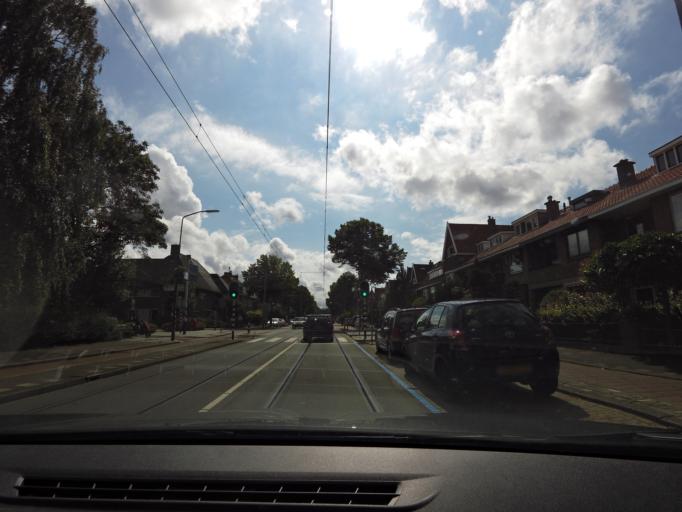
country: NL
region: South Holland
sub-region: Gemeente Leidschendam-Voorburg
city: Voorburg
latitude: 52.0630
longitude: 4.3500
